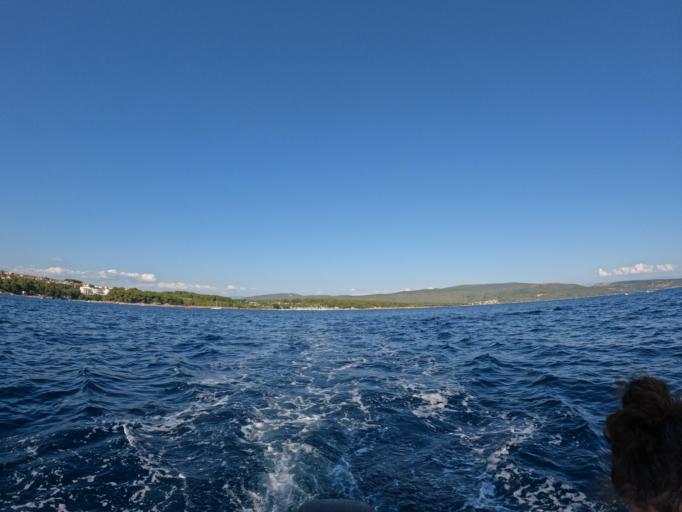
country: HR
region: Primorsko-Goranska
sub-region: Grad Krk
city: Krk
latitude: 45.0196
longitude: 14.5805
